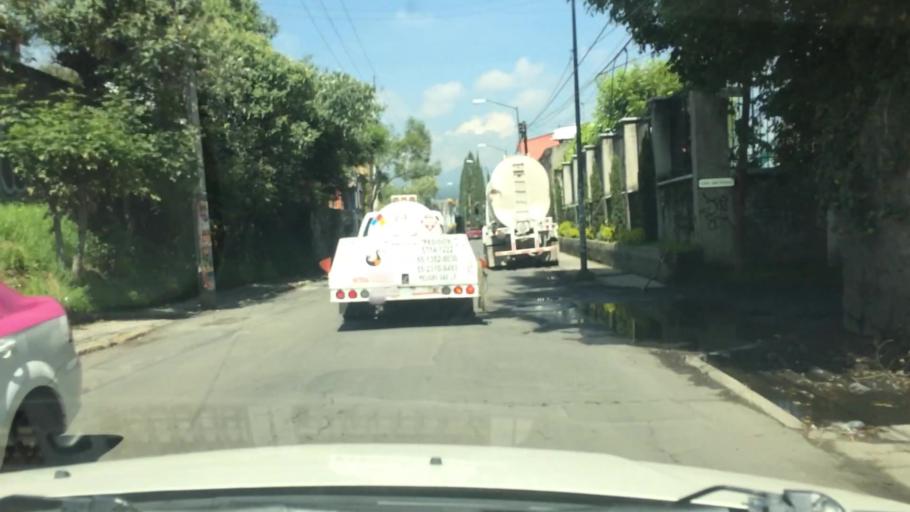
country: MX
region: Mexico City
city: Tlalpan
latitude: 19.2346
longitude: -99.1705
